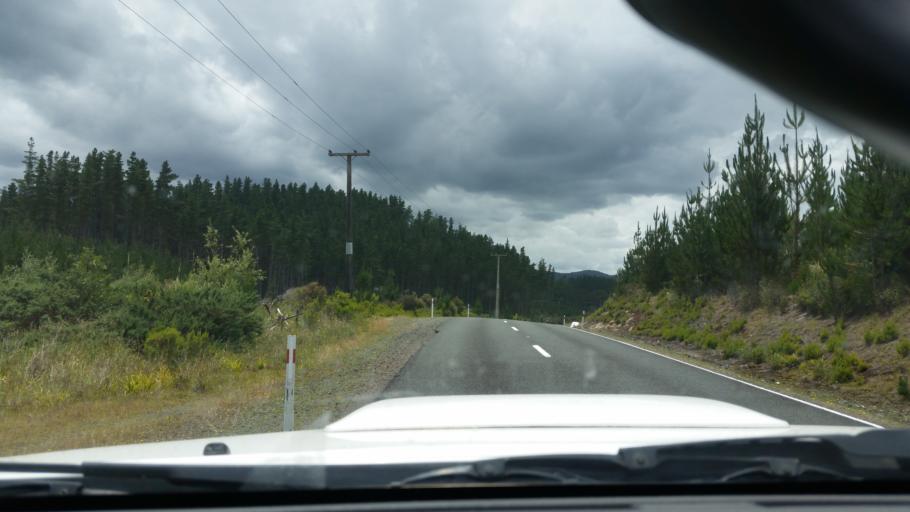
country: NZ
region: Northland
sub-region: Kaipara District
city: Dargaville
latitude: -35.8179
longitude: 173.7120
